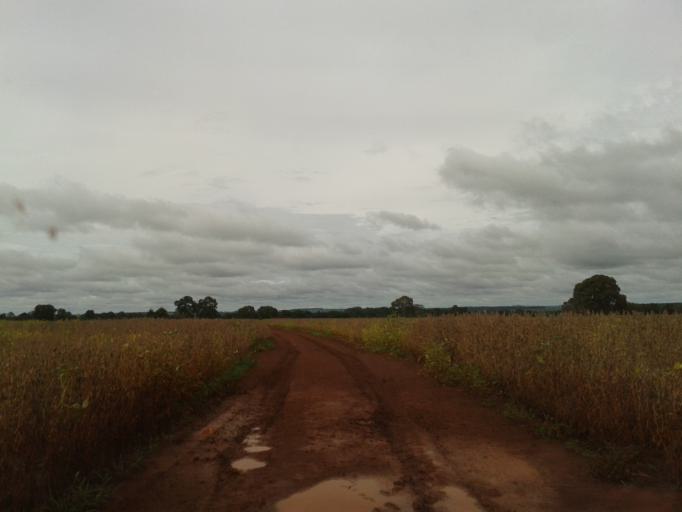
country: BR
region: Minas Gerais
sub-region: Capinopolis
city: Capinopolis
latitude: -18.7769
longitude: -49.7679
